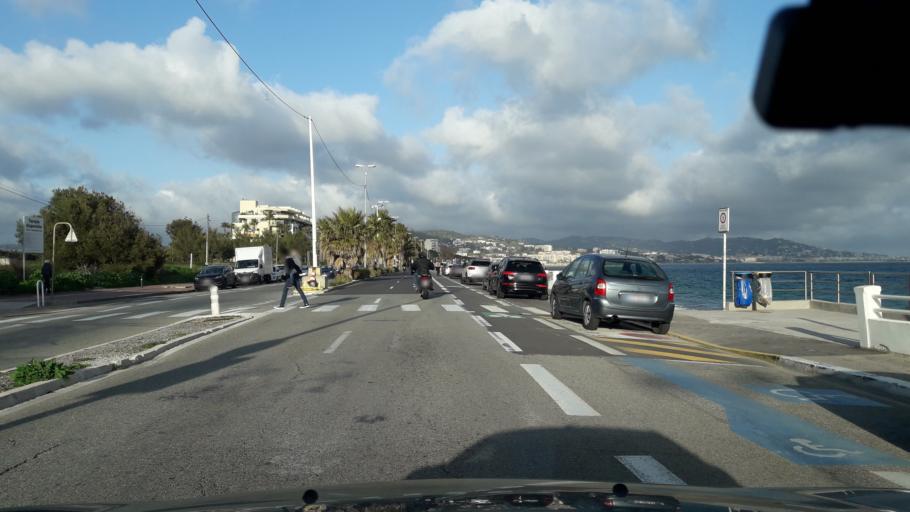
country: FR
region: Provence-Alpes-Cote d'Azur
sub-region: Departement des Alpes-Maritimes
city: Mandelieu-la-Napoule
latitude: 43.5389
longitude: 6.9567
